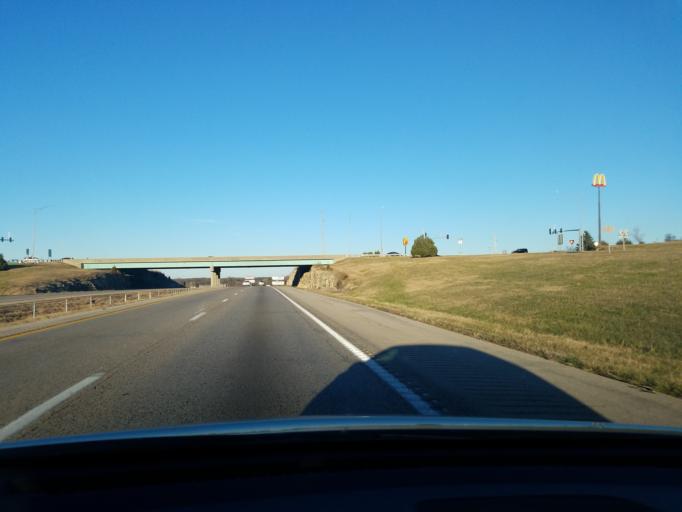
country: US
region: Missouri
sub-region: Franklin County
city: Saint Clair
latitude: 38.3607
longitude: -90.9799
